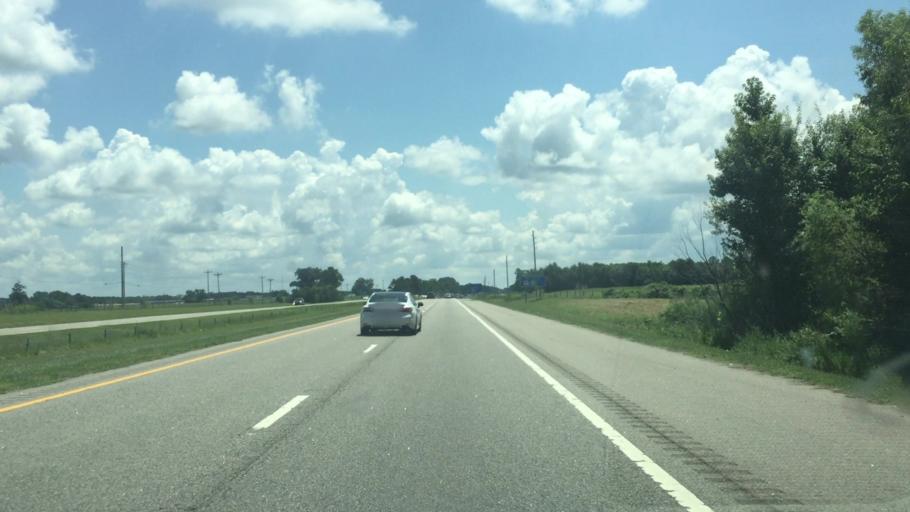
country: US
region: North Carolina
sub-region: Robeson County
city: Lumberton
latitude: 34.5887
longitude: -79.0659
